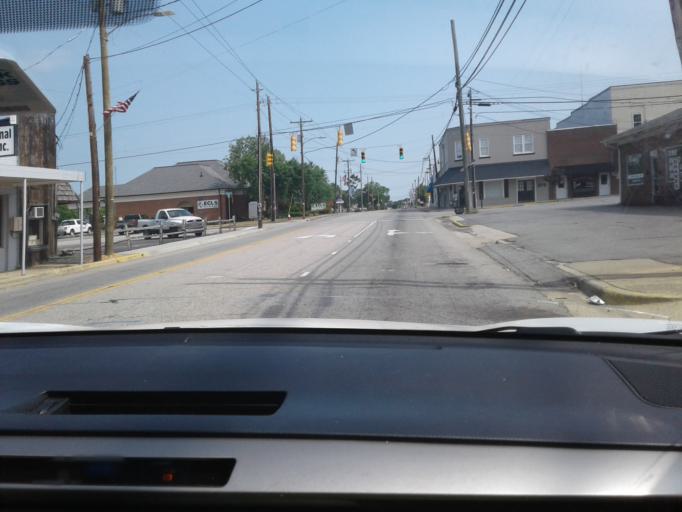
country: US
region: North Carolina
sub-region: Harnett County
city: Coats
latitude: 35.4074
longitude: -78.6724
